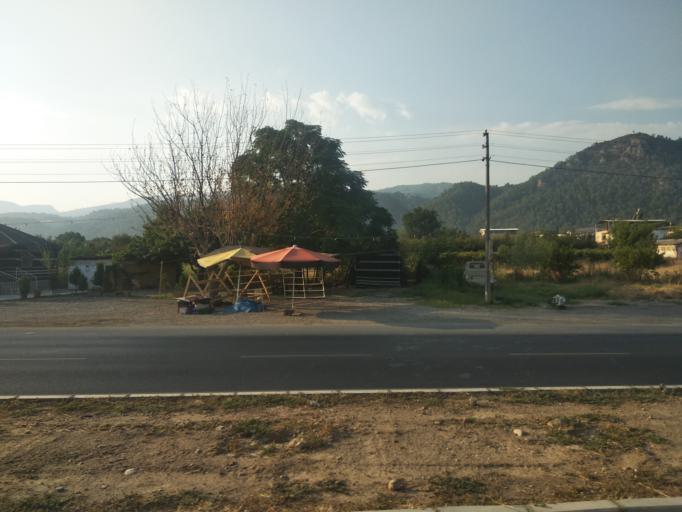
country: TR
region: Manisa
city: Ahmetli
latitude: 38.5014
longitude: 27.8723
